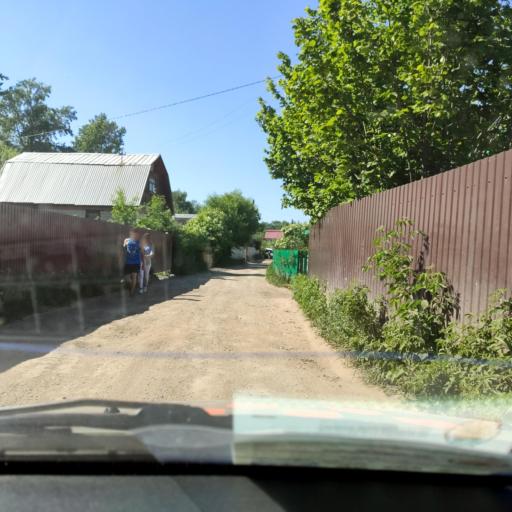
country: RU
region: Bashkortostan
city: Ufa
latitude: 54.7861
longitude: 56.1852
